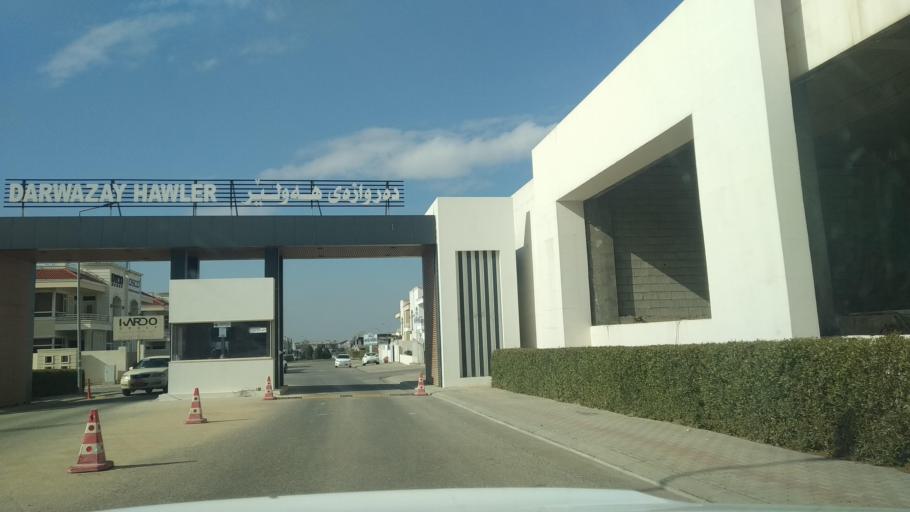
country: IQ
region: Arbil
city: Erbil
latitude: 36.2636
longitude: 44.0900
